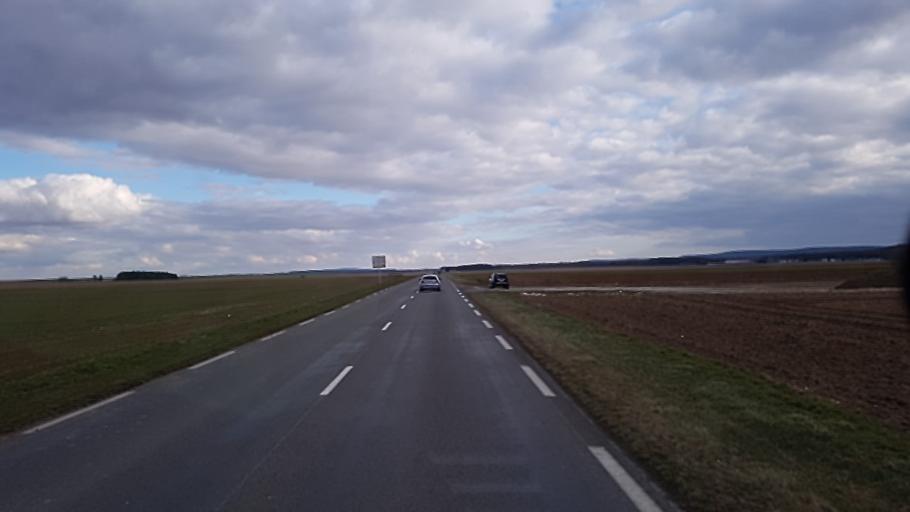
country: FR
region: Picardie
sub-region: Departement de l'Aisne
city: Saint-Erme-Outre-et-Ramecourt
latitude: 49.4487
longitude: 3.8414
